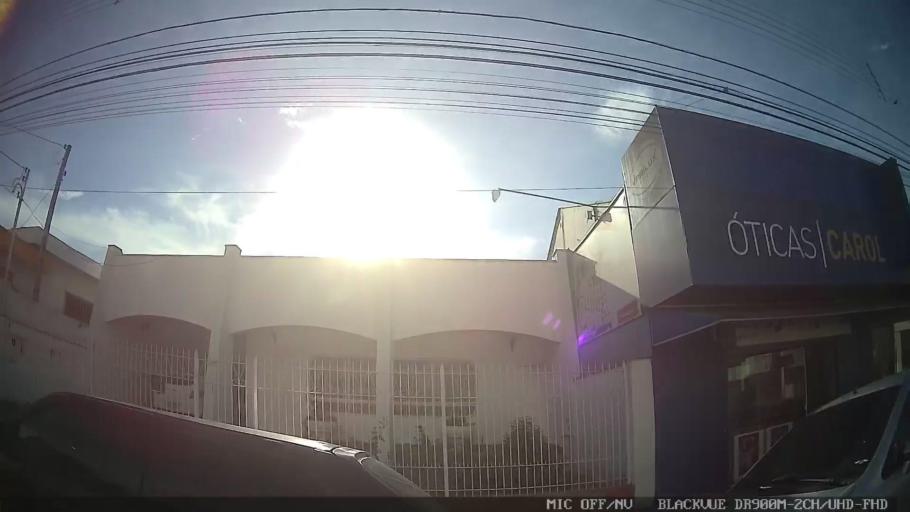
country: BR
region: Sao Paulo
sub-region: Tiete
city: Tiete
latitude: -23.1007
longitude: -47.7155
